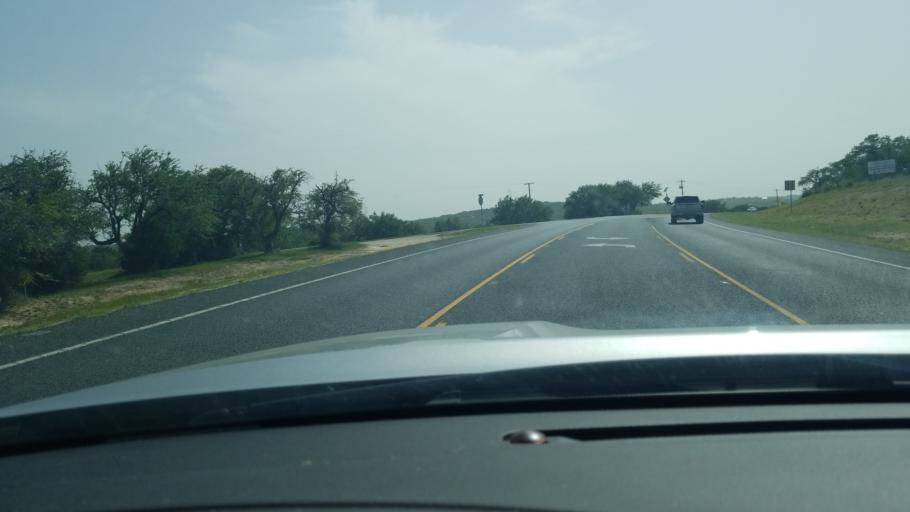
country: US
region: Texas
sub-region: Comal County
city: Bulverde
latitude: 29.7919
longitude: -98.4659
